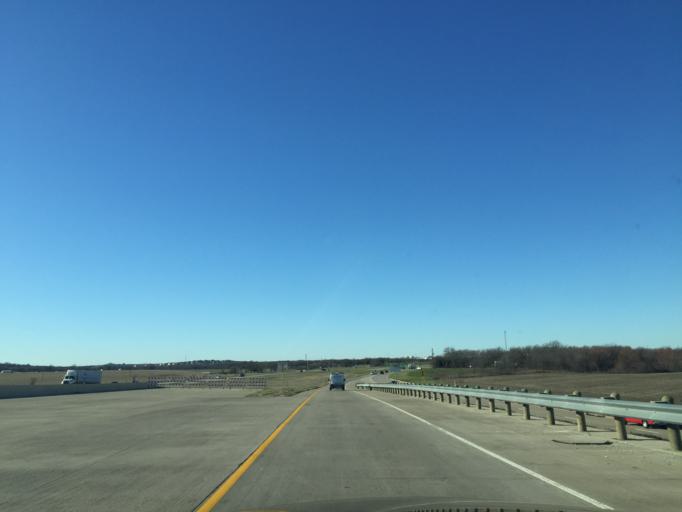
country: US
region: Texas
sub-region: Denton County
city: Roanoke
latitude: 32.9905
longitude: -97.2249
